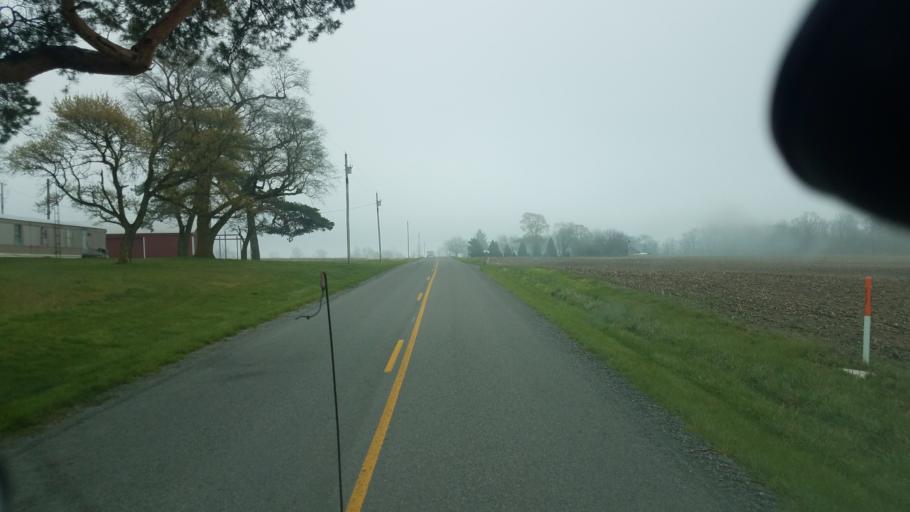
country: US
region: Ohio
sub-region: Logan County
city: Bellefontaine
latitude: 40.4061
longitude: -83.8248
